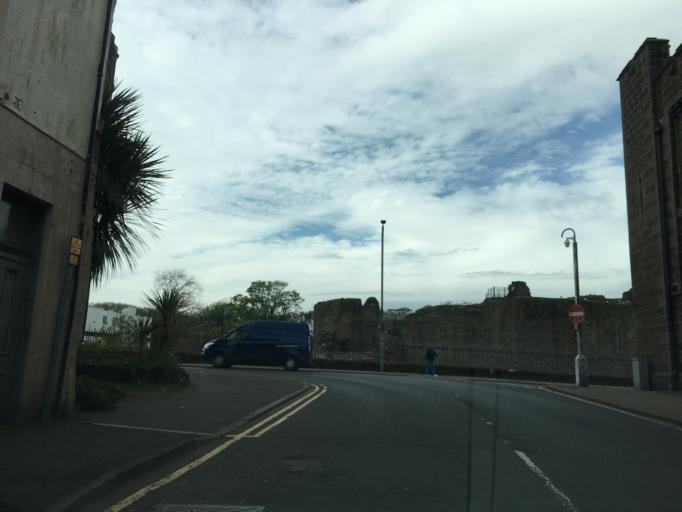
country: GB
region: Scotland
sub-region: Argyll and Bute
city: Rothesay
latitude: 55.8363
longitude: -5.0535
